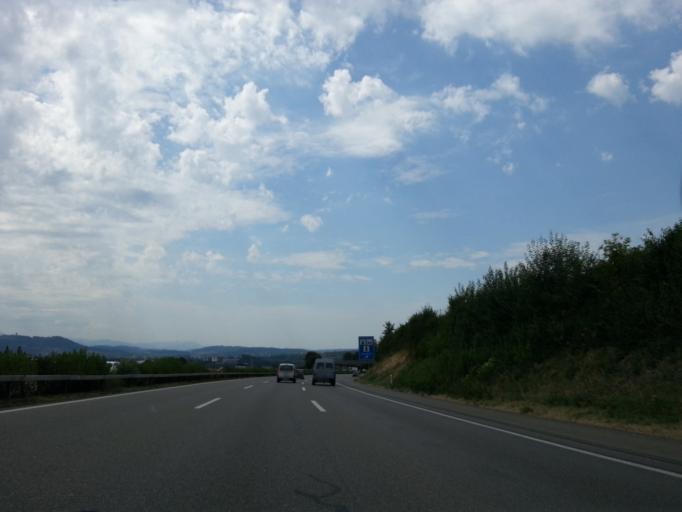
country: CH
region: Bern
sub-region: Bern-Mittelland District
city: Bolligen
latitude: 46.9922
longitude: 7.4815
